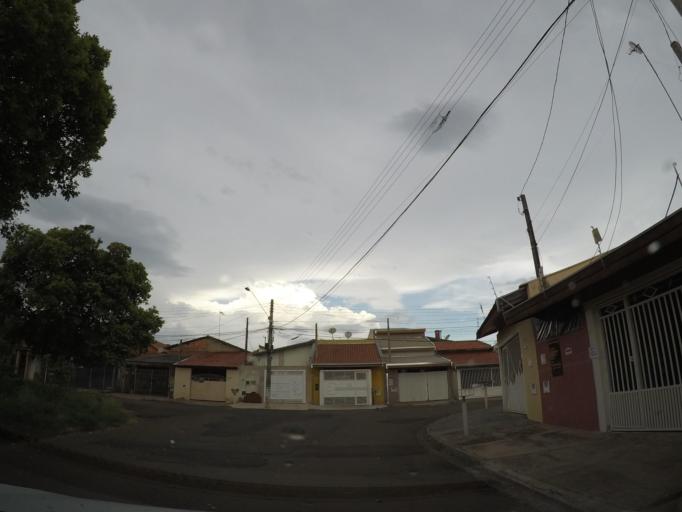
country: BR
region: Sao Paulo
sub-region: Sumare
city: Sumare
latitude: -22.8123
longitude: -47.2502
